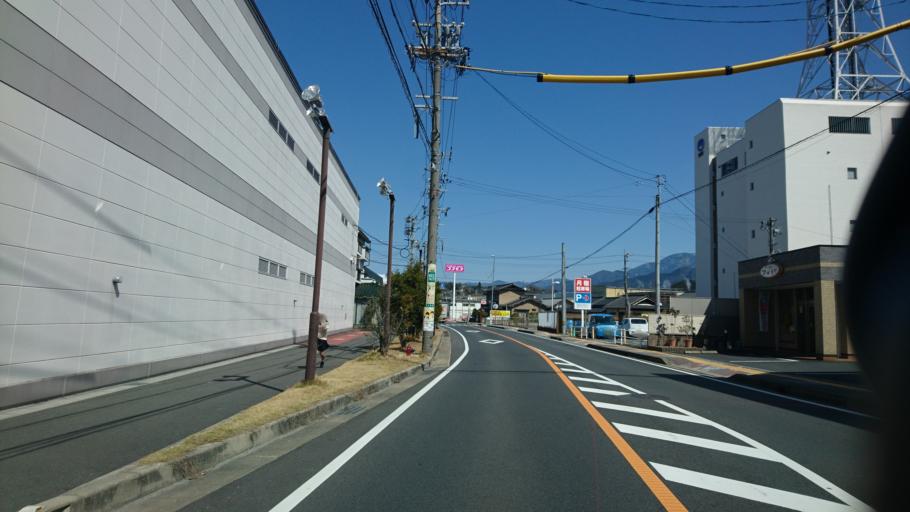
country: JP
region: Gifu
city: Nakatsugawa
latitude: 35.4519
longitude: 137.4110
